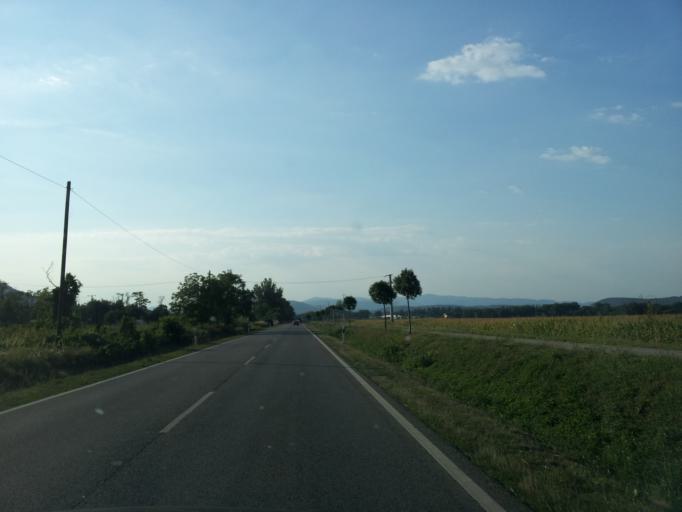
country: HU
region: Pest
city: Dunabogdany
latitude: 47.7783
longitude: 19.0528
